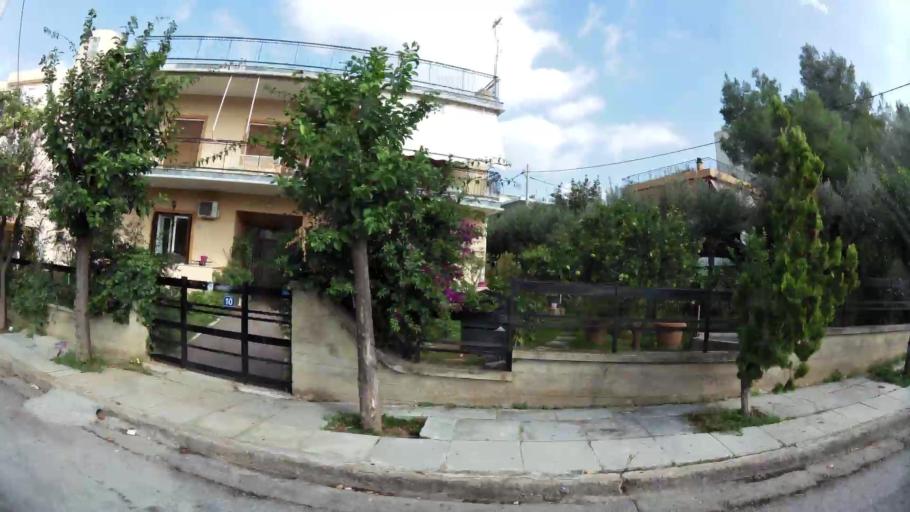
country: GR
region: Attica
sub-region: Nomarchia Athinas
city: Papagou
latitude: 37.9848
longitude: 23.7948
